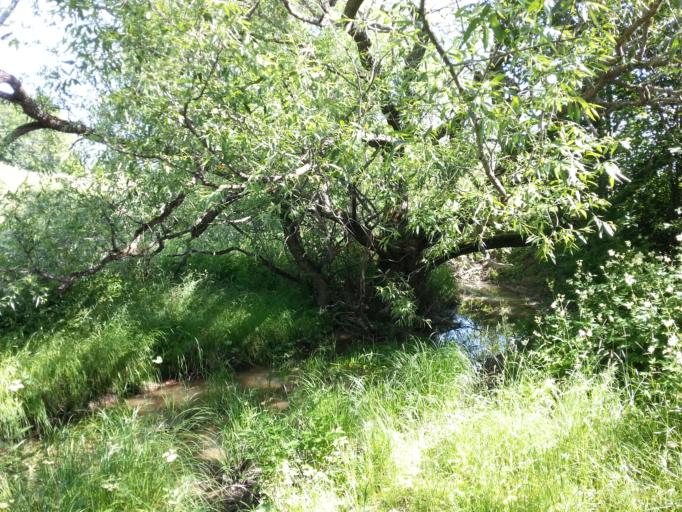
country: SE
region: Uppsala
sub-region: Uppsala Kommun
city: Uppsala
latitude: 59.8669
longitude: 17.5905
